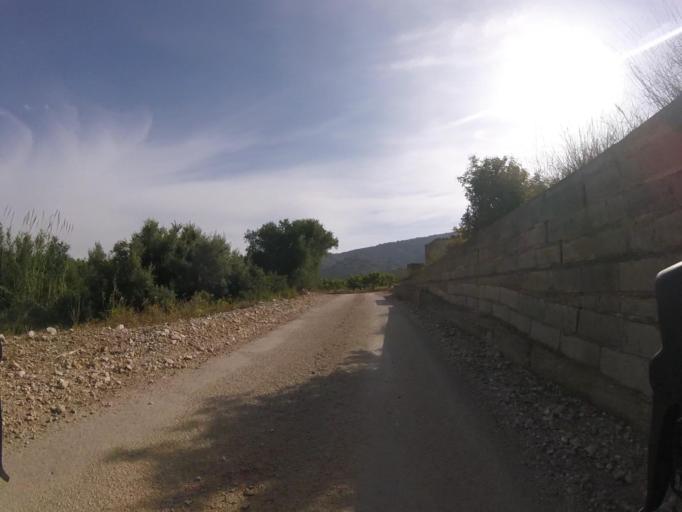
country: ES
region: Valencia
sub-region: Provincia de Castello
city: Alcala de Xivert
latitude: 40.2823
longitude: 0.2644
